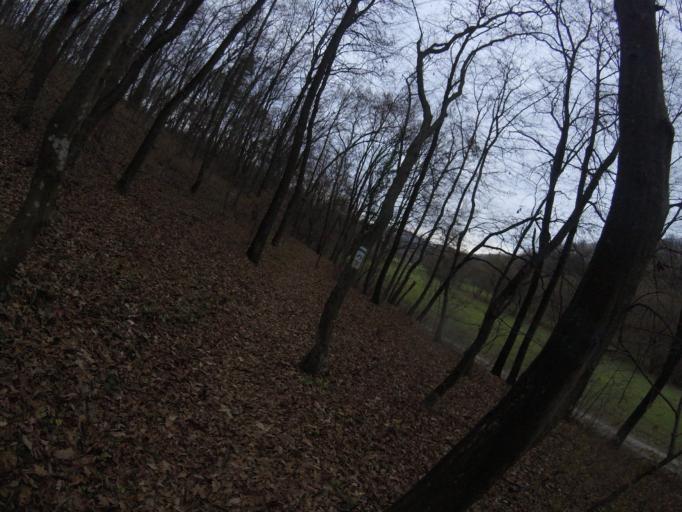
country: HU
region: Tolna
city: Szentgalpuszta
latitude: 46.3369
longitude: 18.6176
